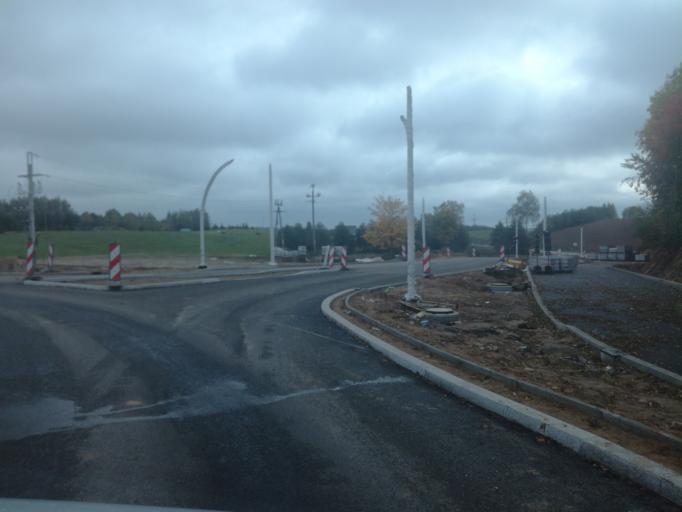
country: PL
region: Podlasie
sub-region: Powiat sejnenski
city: Sejny
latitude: 54.1063
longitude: 23.4100
